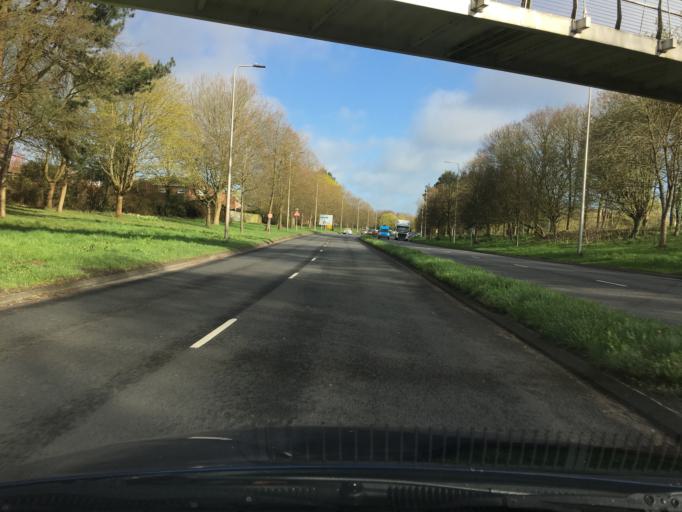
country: GB
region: England
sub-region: Bracknell Forest
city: Bracknell
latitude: 51.4001
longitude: -0.7621
